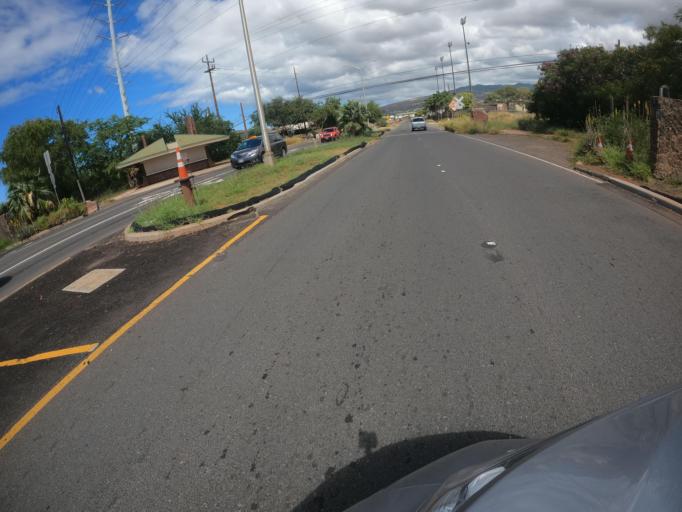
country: US
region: Hawaii
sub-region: Honolulu County
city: Makakilo City
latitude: 21.3257
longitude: -158.0674
